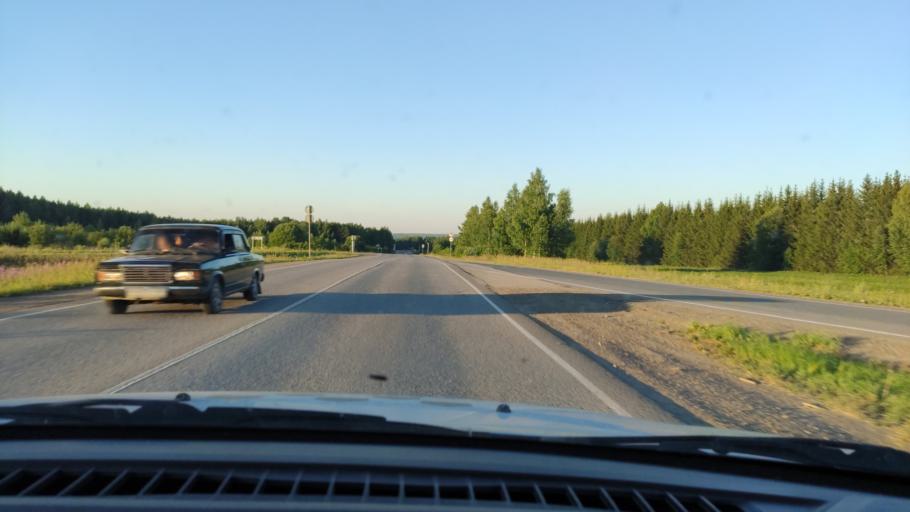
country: RU
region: Perm
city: Kungur
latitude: 57.4055
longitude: 56.8947
